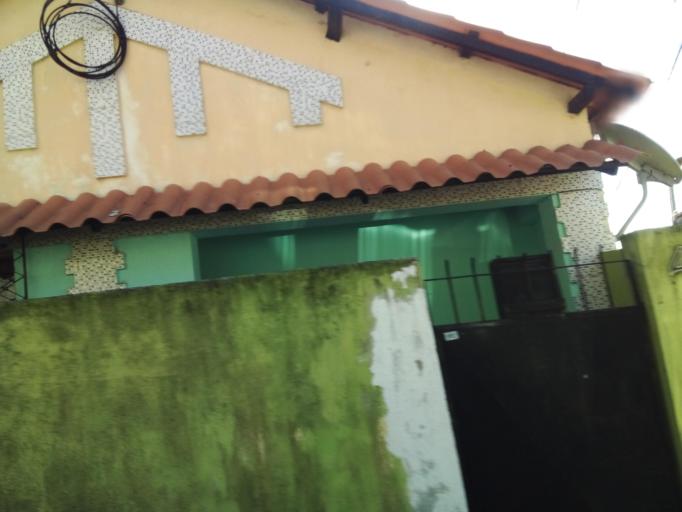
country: BR
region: Espirito Santo
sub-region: Vitoria
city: Vitoria
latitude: -20.3289
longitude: -40.3446
